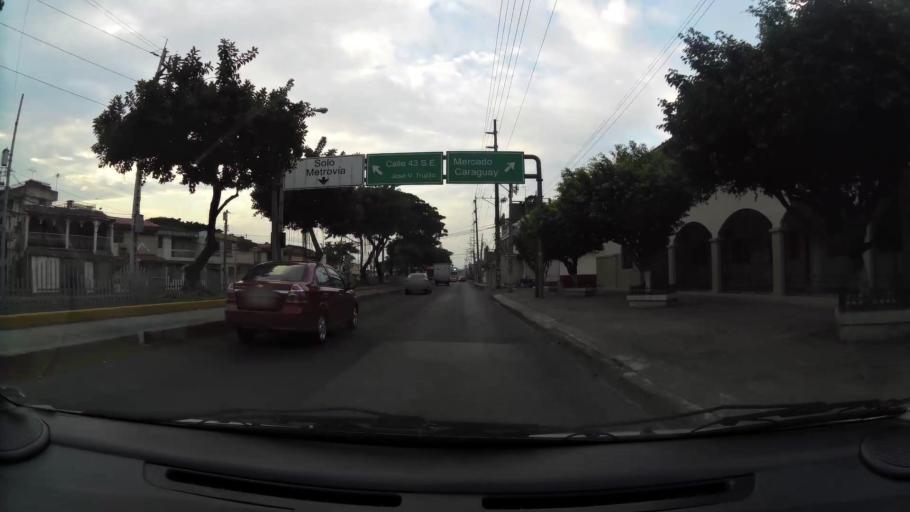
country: EC
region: Guayas
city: Guayaquil
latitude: -2.2287
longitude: -79.8900
